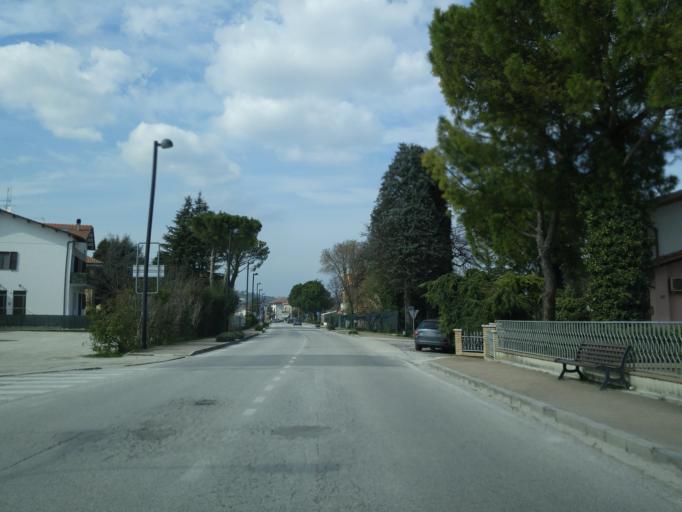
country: IT
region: The Marches
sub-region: Provincia di Pesaro e Urbino
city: Villanova
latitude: 43.7380
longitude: 12.9365
